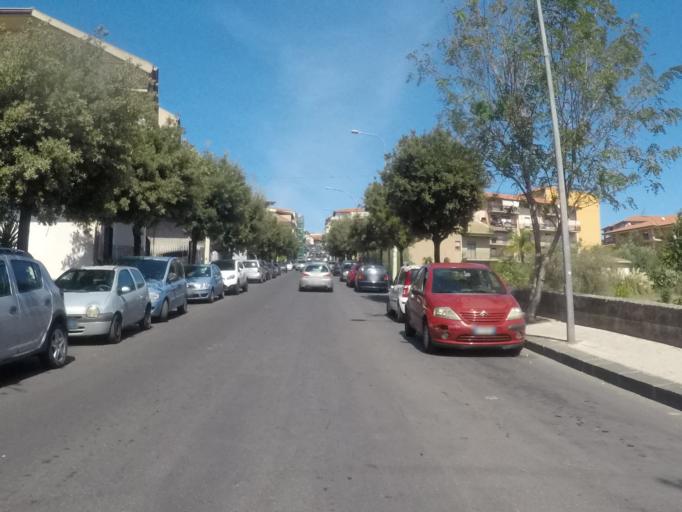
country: IT
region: Sicily
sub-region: Catania
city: Motta Sant'Anastasia
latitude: 37.5128
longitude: 14.9662
